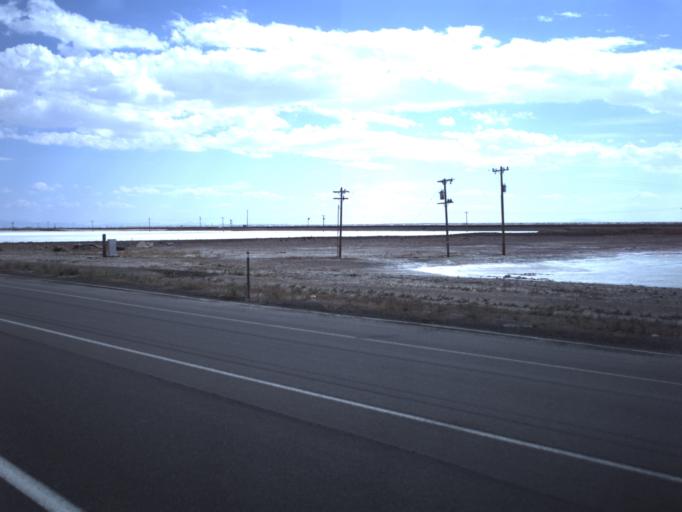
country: US
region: Utah
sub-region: Tooele County
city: Wendover
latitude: 40.7385
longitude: -113.8537
